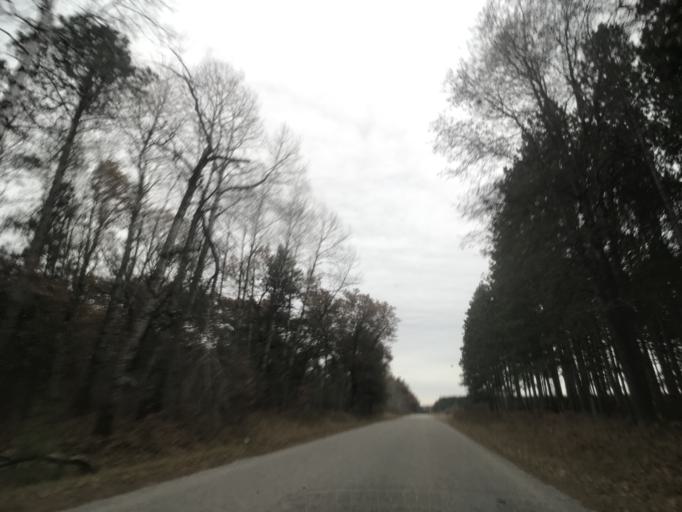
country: US
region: Wisconsin
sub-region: Oconto County
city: Gillett
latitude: 45.3416
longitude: -88.2861
